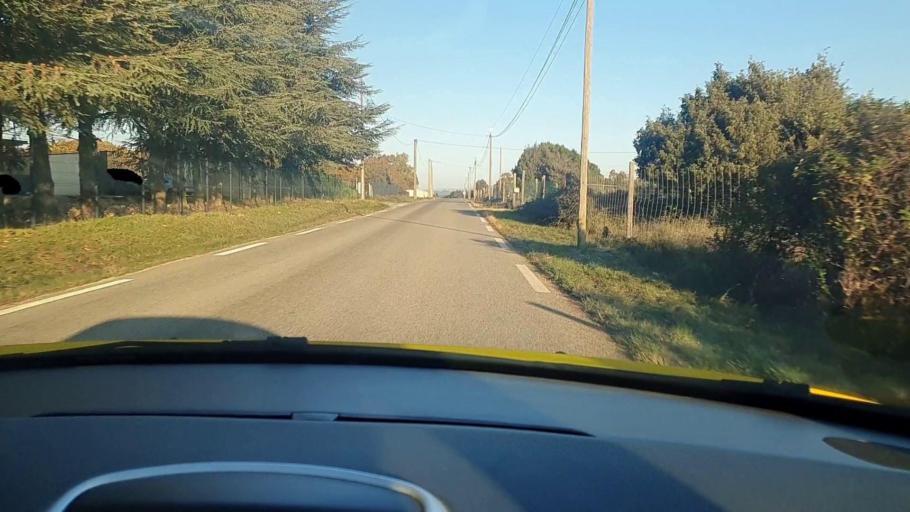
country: FR
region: Languedoc-Roussillon
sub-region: Departement du Gard
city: Montaren-et-Saint-Mediers
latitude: 44.1207
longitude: 4.3687
